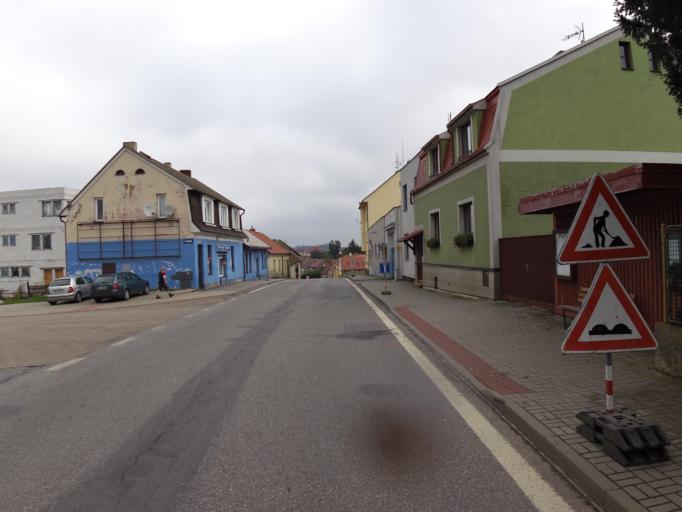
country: CZ
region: Jihocesky
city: Mlada Vozice
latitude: 49.5288
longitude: 14.8066
